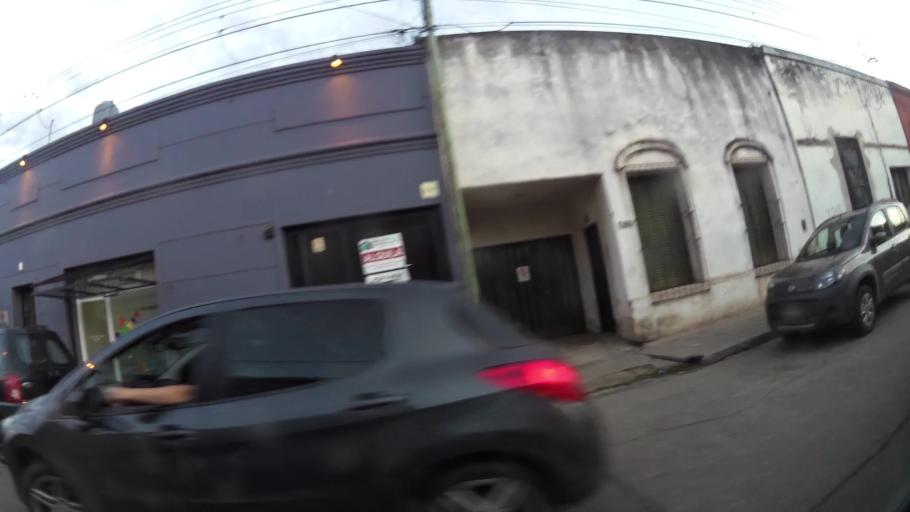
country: AR
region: Buenos Aires
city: San Nicolas de los Arroyos
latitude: -33.3305
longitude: -60.2227
